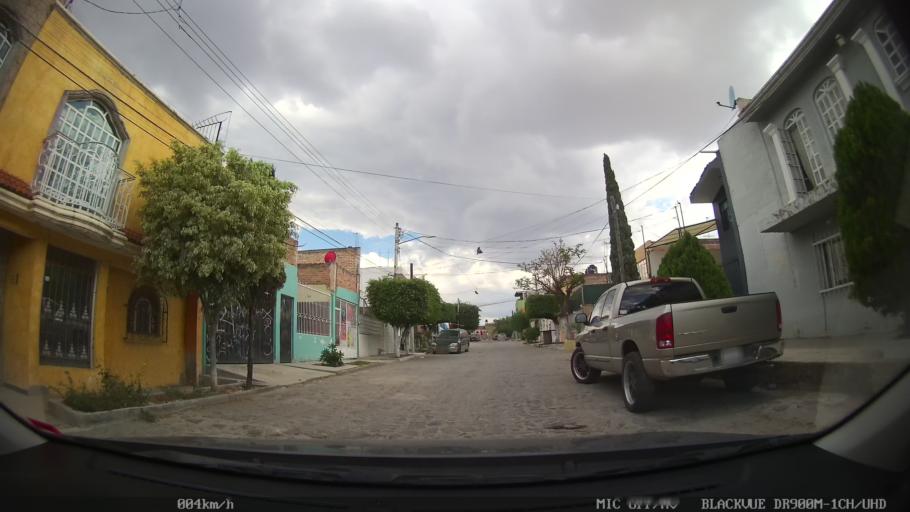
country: MX
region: Jalisco
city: Tlaquepaque
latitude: 20.6873
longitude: -103.2614
